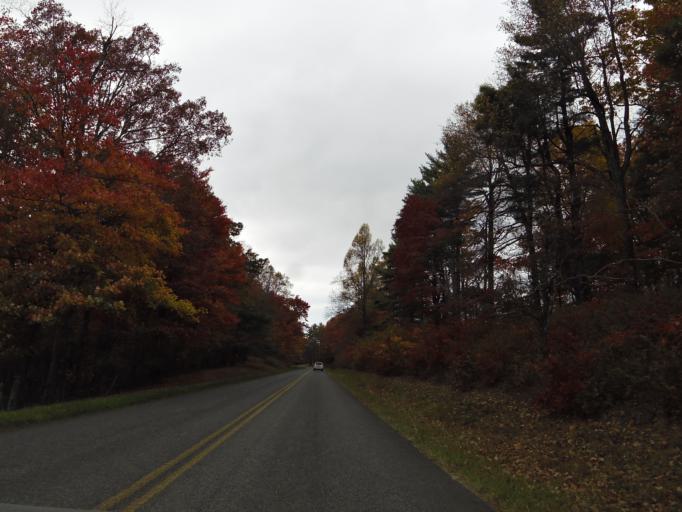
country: US
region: Virginia
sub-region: Carroll County
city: Woodlawn
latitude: 36.6066
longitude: -80.7991
